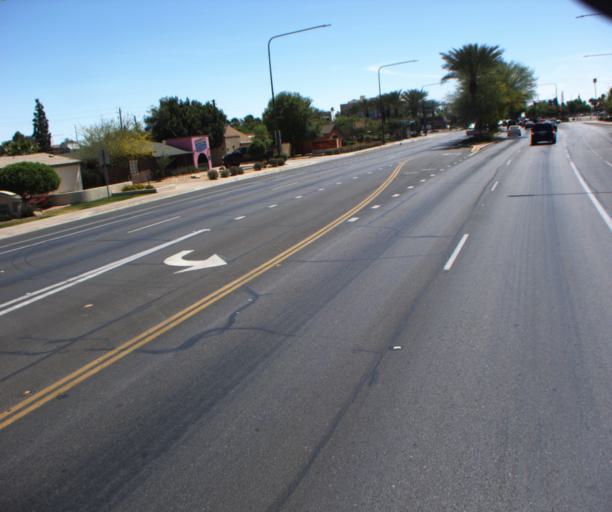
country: US
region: Arizona
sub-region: Maricopa County
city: Chandler
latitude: 33.3079
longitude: -111.8415
